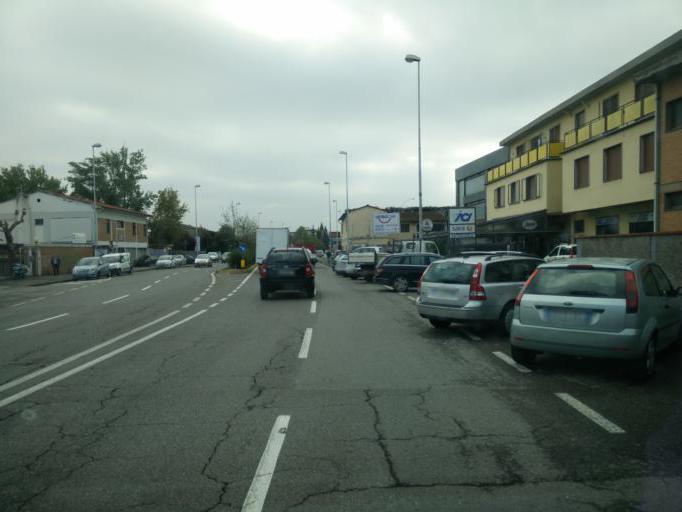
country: IT
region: Tuscany
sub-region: Province of Florence
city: Mantignano-Ugnano
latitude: 43.8023
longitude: 11.1886
